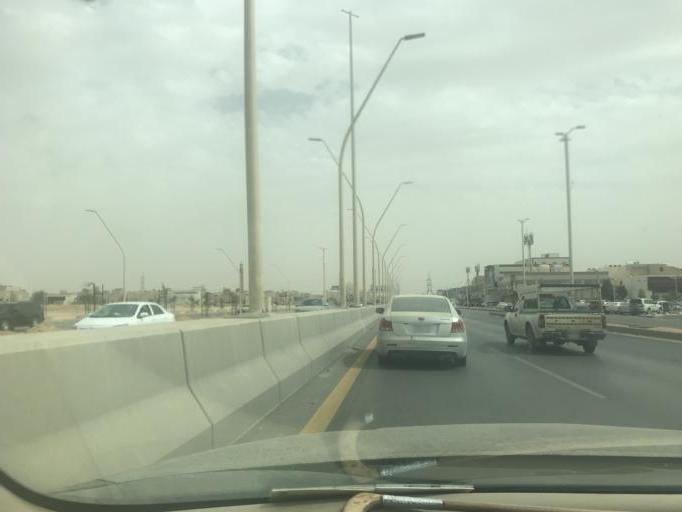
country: SA
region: Ar Riyad
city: Riyadh
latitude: 24.8021
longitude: 46.6740
